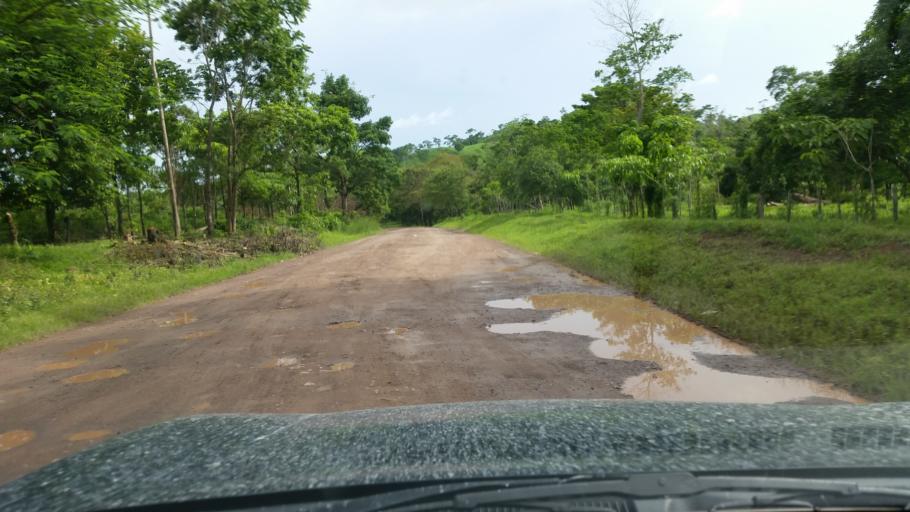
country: NI
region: Atlantico Norte (RAAN)
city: Siuna
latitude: 13.5087
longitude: -84.8434
